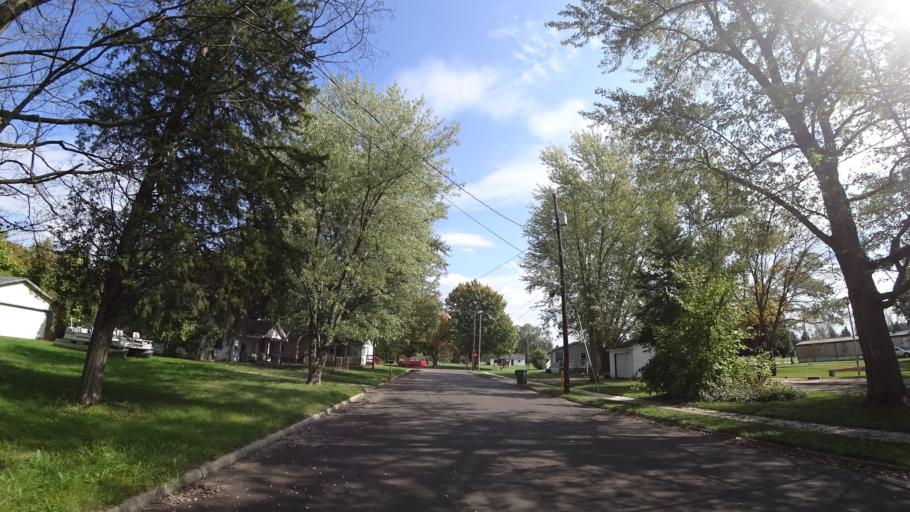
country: US
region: Michigan
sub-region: Saint Joseph County
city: Three Rivers
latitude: 41.9382
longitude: -85.6181
